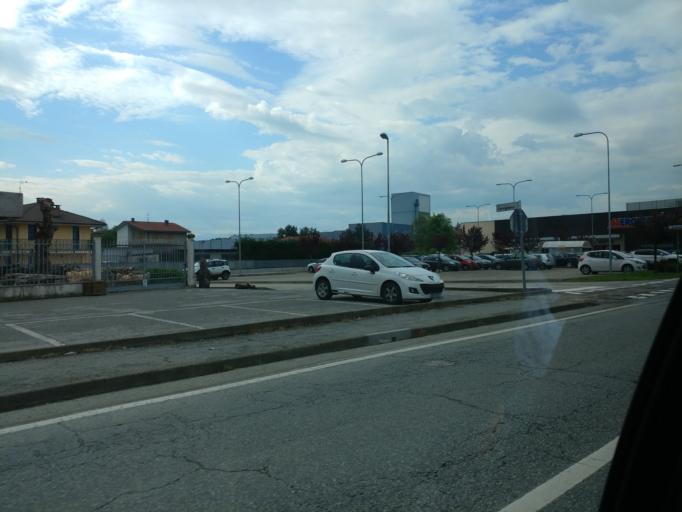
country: IT
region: Piedmont
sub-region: Provincia di Cuneo
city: Moretta
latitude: 44.7555
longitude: 7.5338
